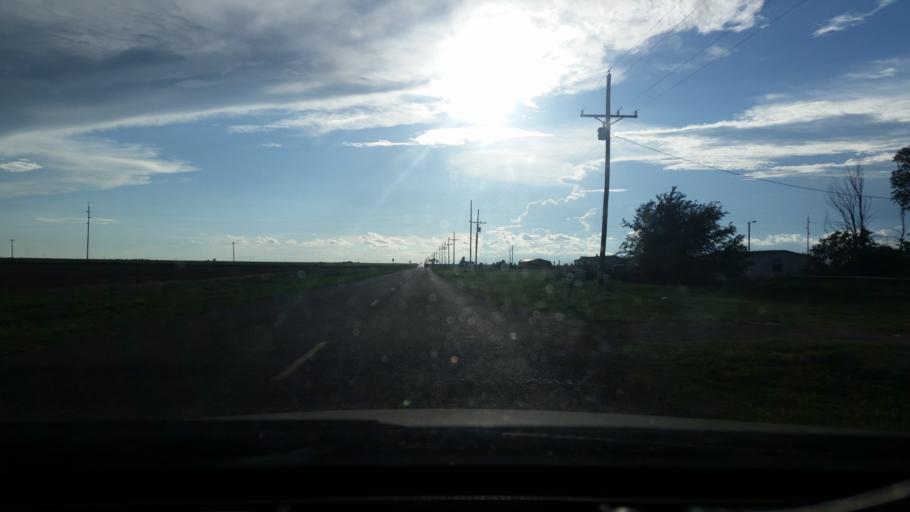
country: US
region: New Mexico
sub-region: Curry County
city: Clovis
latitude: 34.4484
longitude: -103.2107
